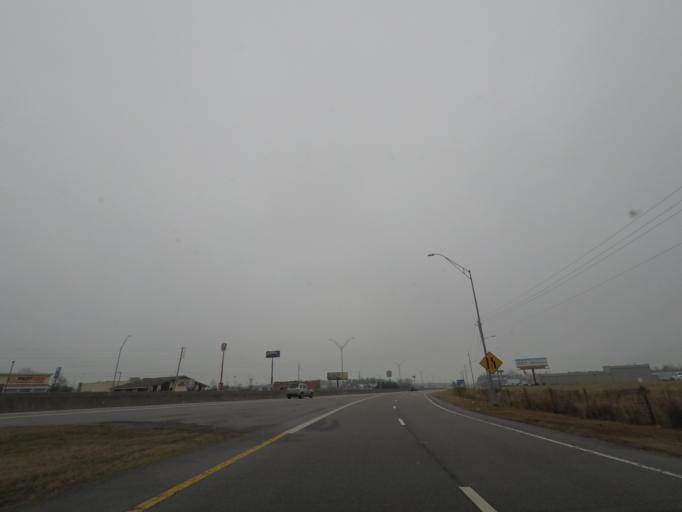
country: US
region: North Carolina
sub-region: Robeson County
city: Lumberton
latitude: 34.6686
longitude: -79.0068
